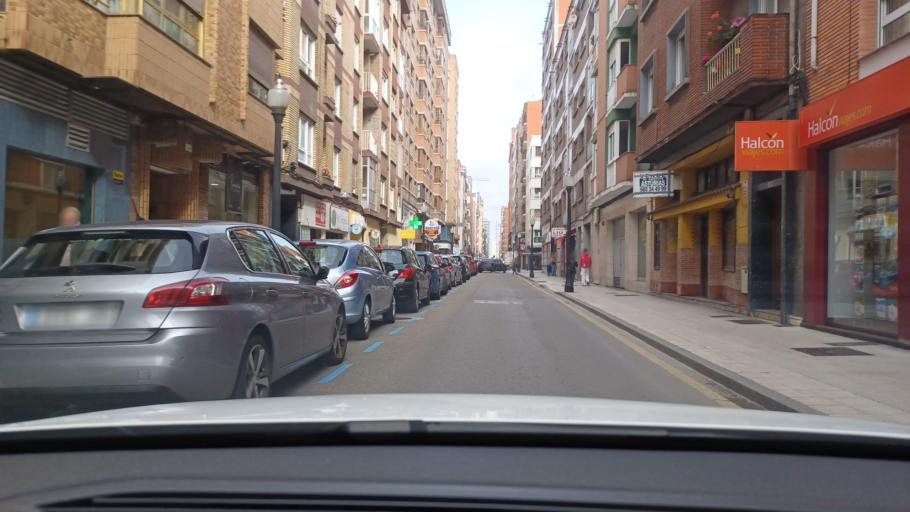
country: ES
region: Asturias
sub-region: Province of Asturias
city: Gijon
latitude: 43.5378
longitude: -5.6489
